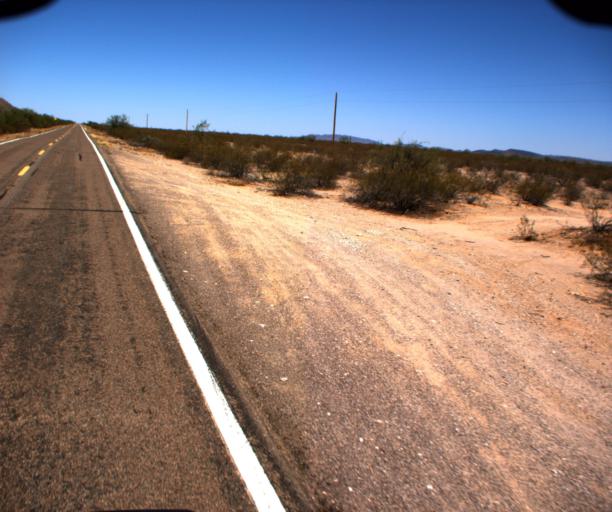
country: US
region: Arizona
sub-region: Pima County
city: Ajo
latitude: 32.2020
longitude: -112.5095
